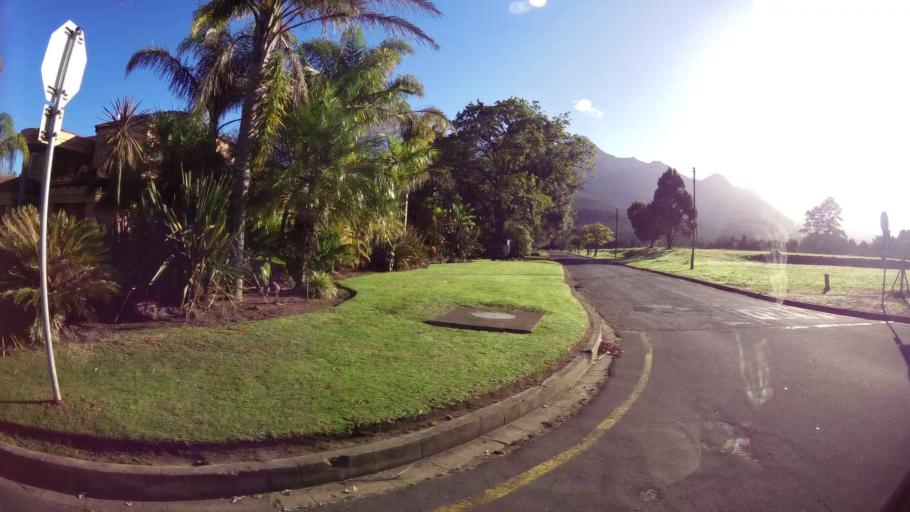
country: ZA
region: Western Cape
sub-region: Eden District Municipality
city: George
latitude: -33.9471
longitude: 22.4495
